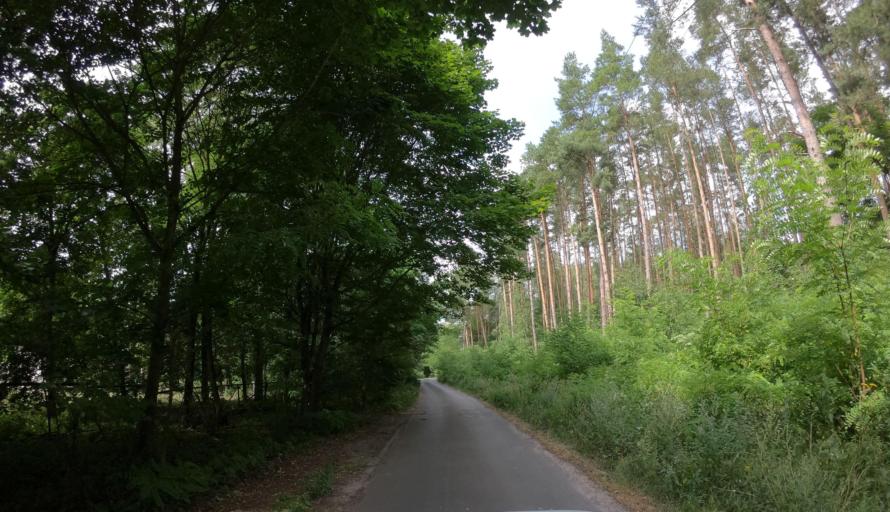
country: PL
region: West Pomeranian Voivodeship
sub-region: Powiat gryfinski
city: Stare Czarnowo
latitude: 53.3442
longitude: 14.7857
